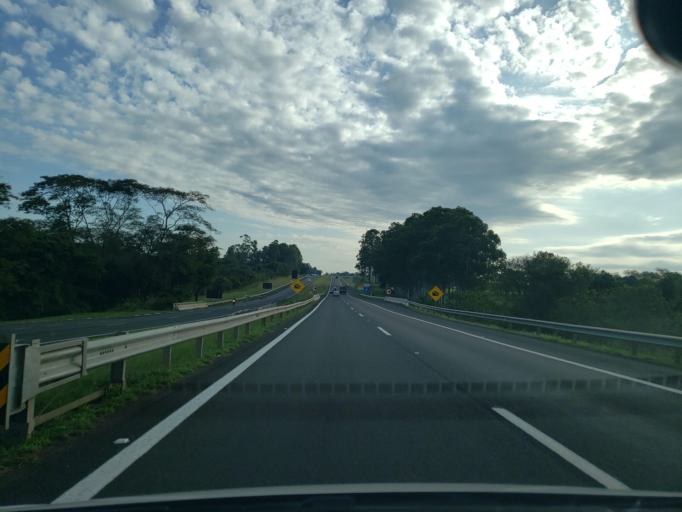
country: BR
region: Sao Paulo
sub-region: Guararapes
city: Guararapes
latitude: -21.2075
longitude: -50.6503
